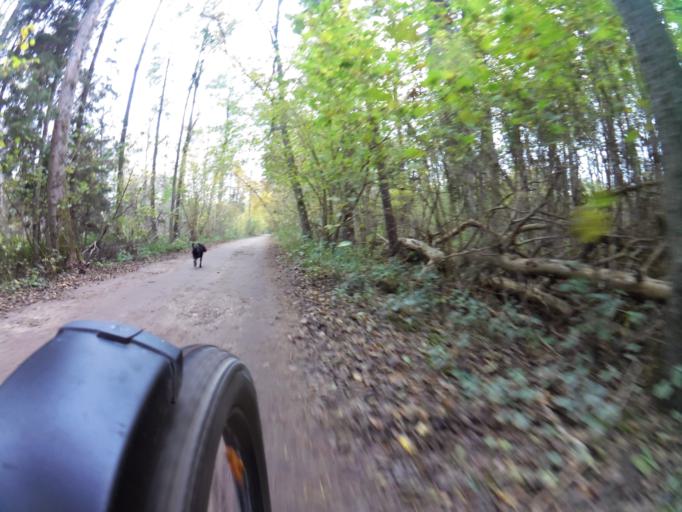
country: PL
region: Pomeranian Voivodeship
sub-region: Powiat pucki
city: Krokowa
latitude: 54.8294
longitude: 18.1145
